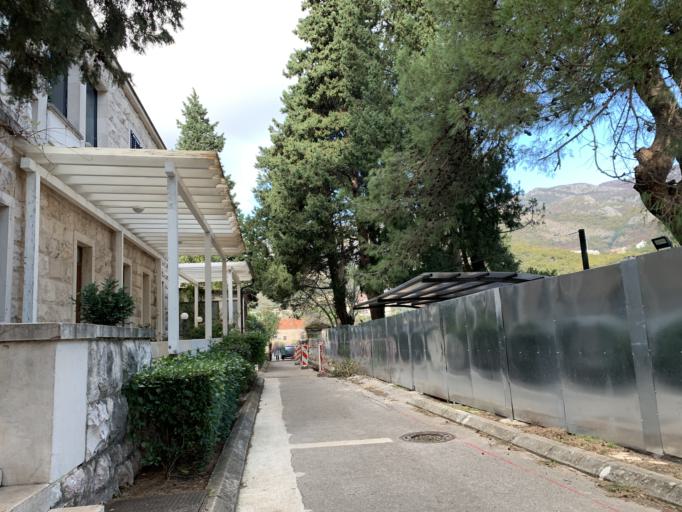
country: ME
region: Budva
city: Budva
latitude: 42.2658
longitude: 18.8919
